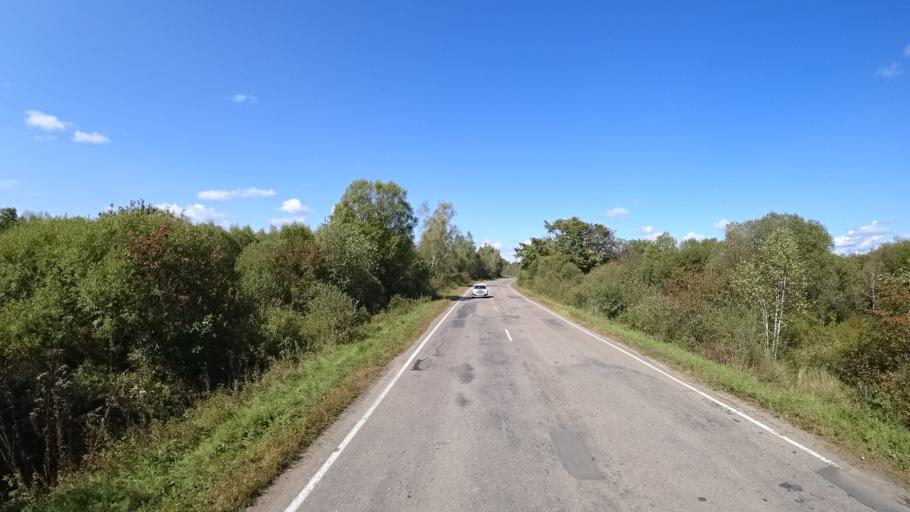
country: RU
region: Amur
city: Arkhara
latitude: 49.4018
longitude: 130.1294
